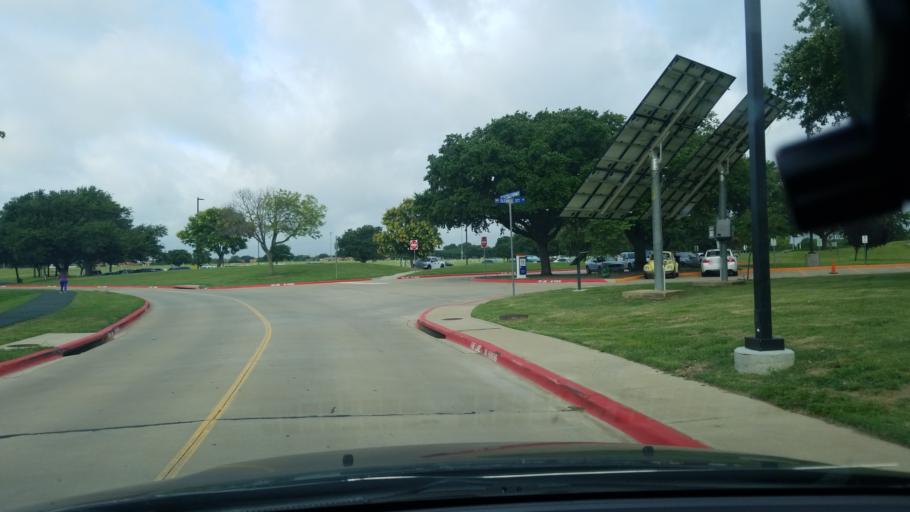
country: US
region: Texas
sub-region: Dallas County
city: Mesquite
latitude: 32.8141
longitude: -96.6592
